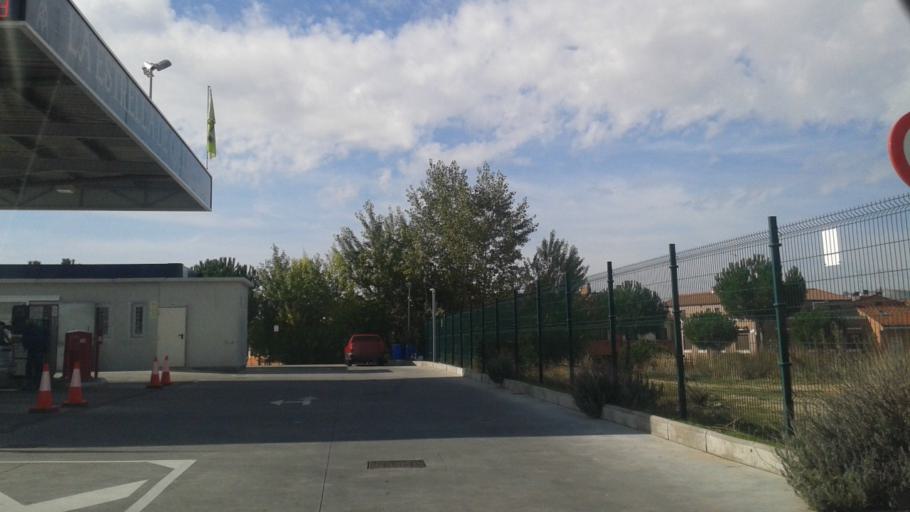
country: ES
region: Castille and Leon
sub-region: Provincia de Valladolid
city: Arroyo
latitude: 41.6285
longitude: -4.7691
